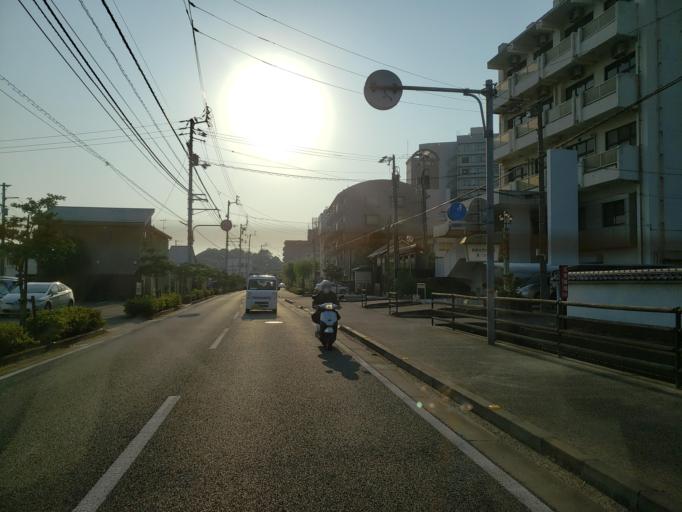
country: JP
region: Ehime
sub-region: Shikoku-chuo Shi
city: Matsuyama
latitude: 33.8474
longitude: 132.7924
